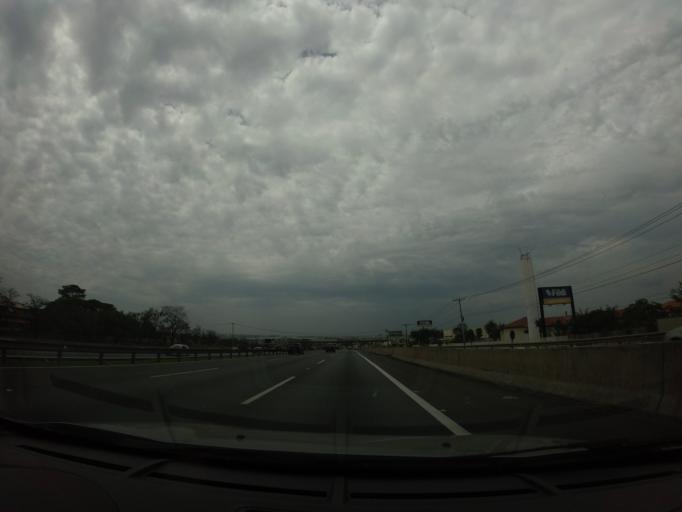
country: BR
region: Sao Paulo
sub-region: Sumare
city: Sumare
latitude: -22.7966
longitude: -47.2242
